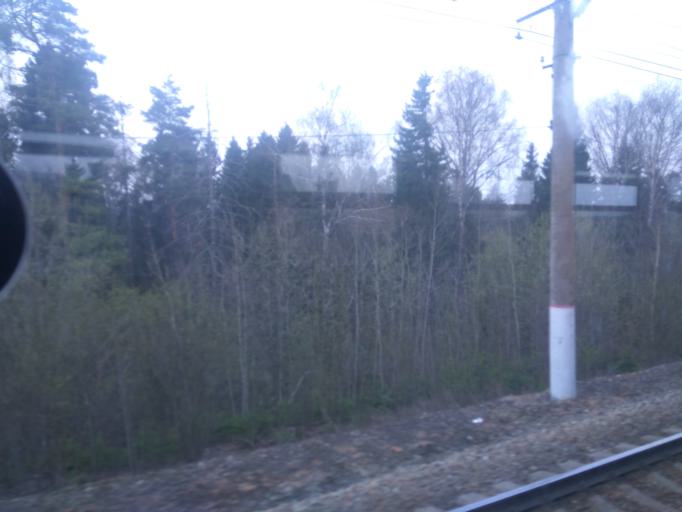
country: RU
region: Moskovskaya
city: Svatkovo
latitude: 56.3872
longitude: 38.2770
